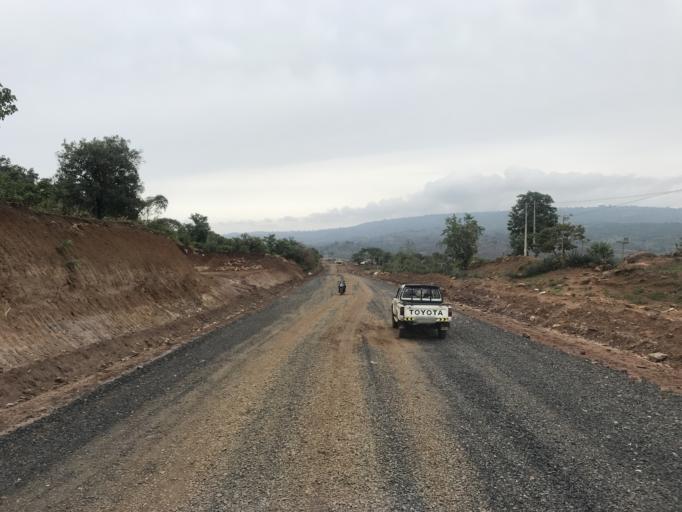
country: ET
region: Oromiya
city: Shambu
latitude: 10.0777
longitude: 36.8810
